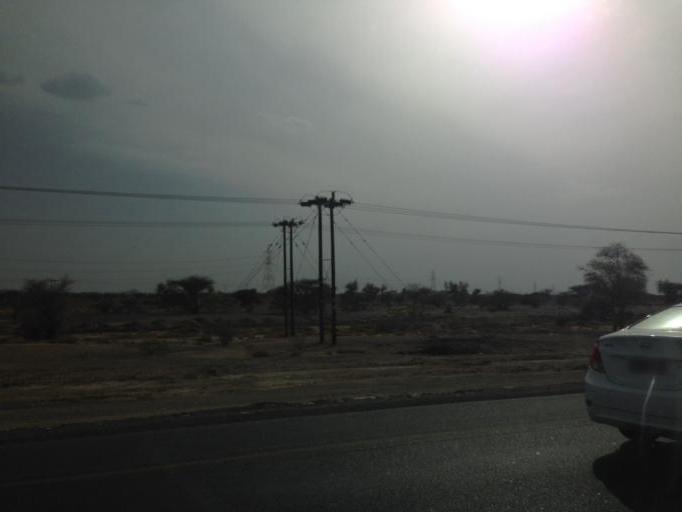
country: OM
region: Ash Sharqiyah
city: Al Qabil
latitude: 22.5987
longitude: 58.6720
